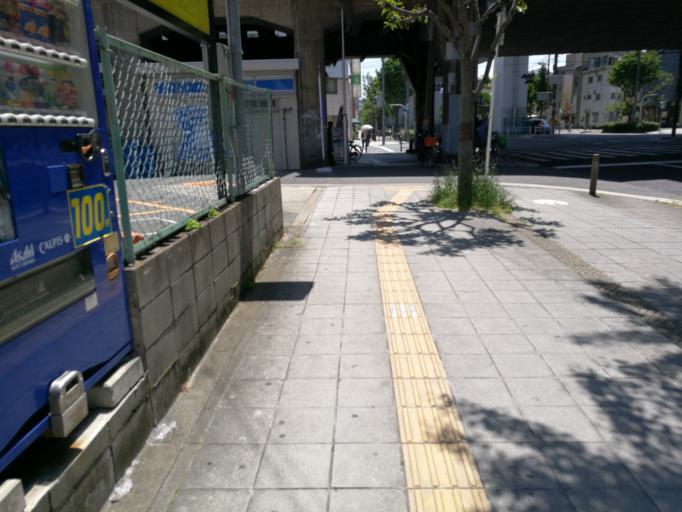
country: JP
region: Osaka
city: Osaka-shi
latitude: 34.6915
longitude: 135.4777
